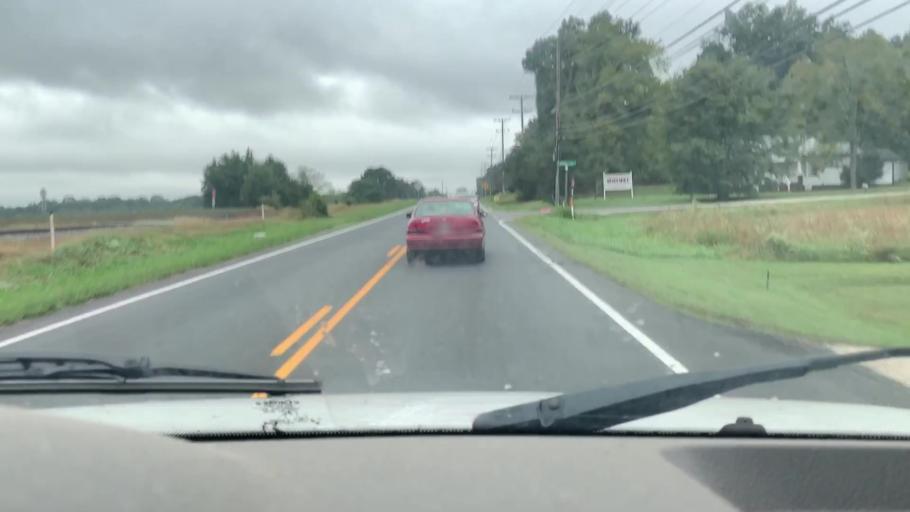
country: US
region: North Carolina
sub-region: Gaston County
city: Davidson
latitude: 35.5187
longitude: -80.8407
